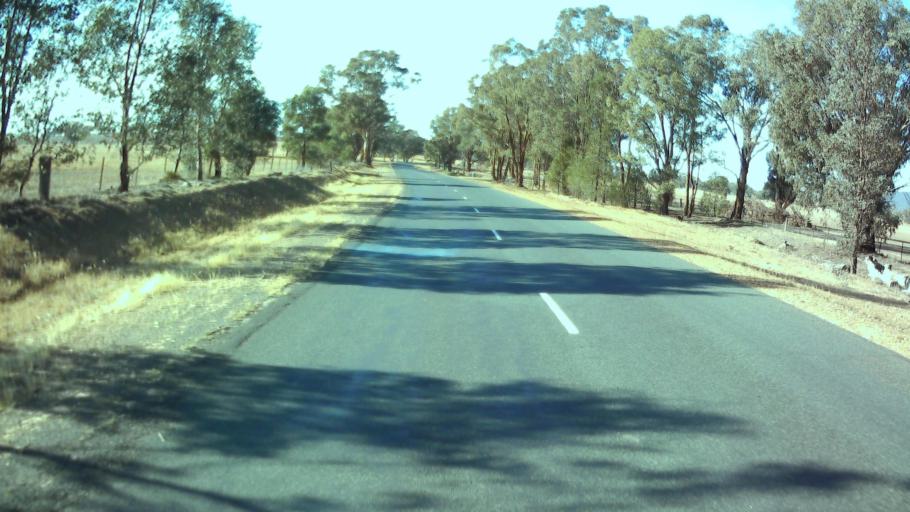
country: AU
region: New South Wales
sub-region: Weddin
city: Grenfell
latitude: -33.9314
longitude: 148.1374
